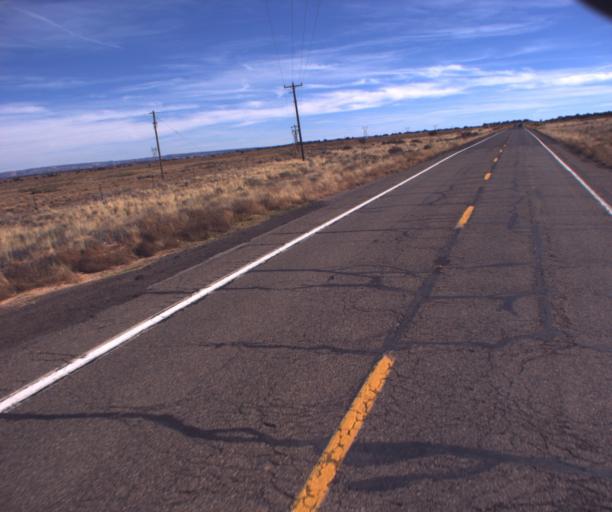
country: US
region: Arizona
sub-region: Coconino County
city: Kaibito
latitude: 36.6163
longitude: -110.9463
